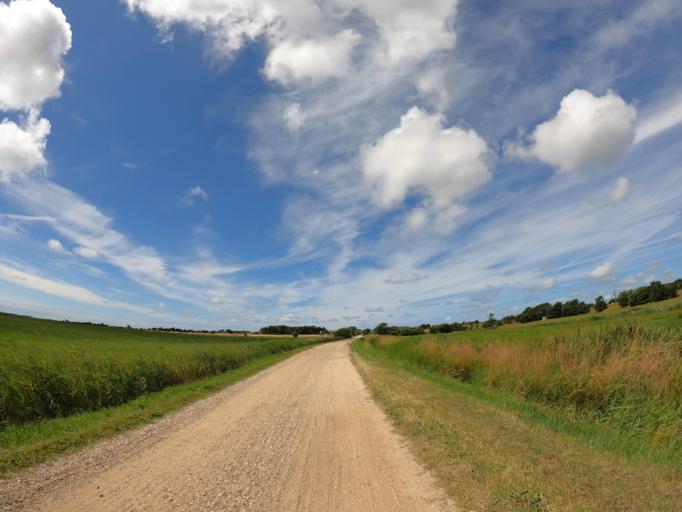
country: DE
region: Schleswig-Holstein
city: Tinnum
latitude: 54.8942
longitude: 8.3490
